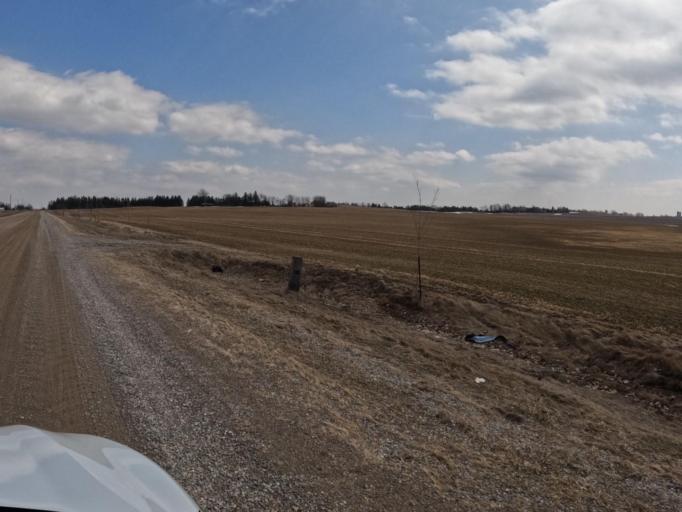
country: CA
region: Ontario
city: Shelburne
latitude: 44.0665
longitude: -80.2101
